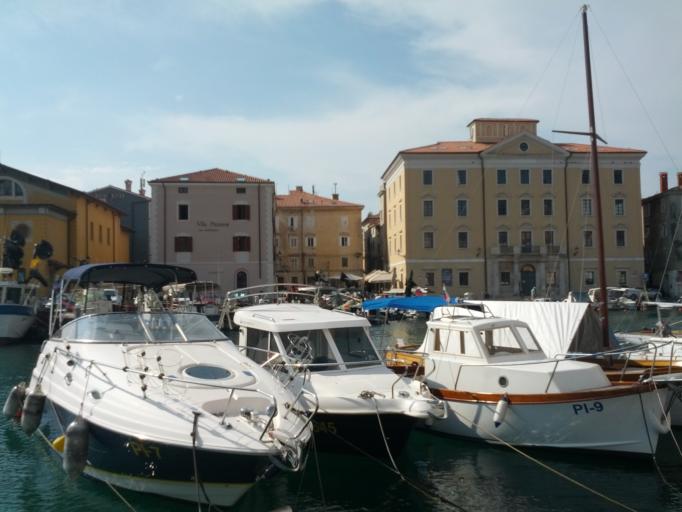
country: SI
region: Piran-Pirano
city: Piran
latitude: 45.5274
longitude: 13.5679
